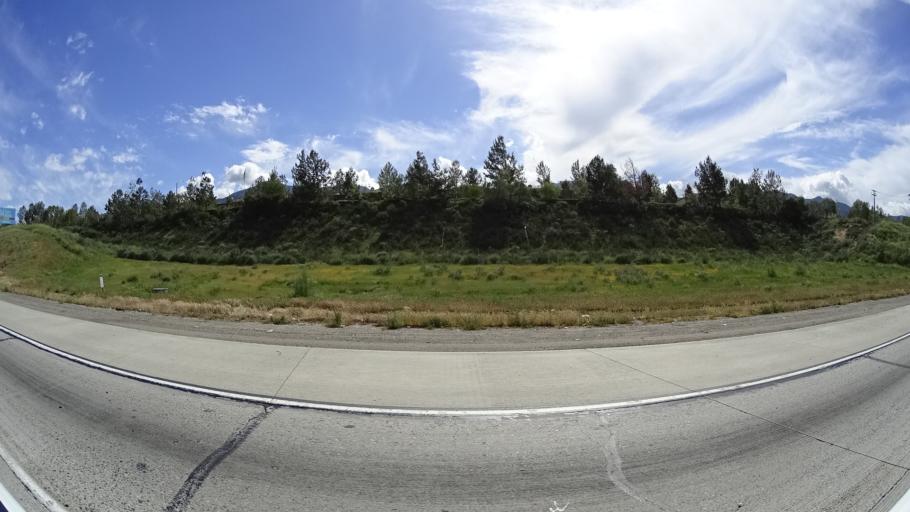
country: US
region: California
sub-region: Riverside County
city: El Cerrito
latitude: 33.7566
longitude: -117.4609
